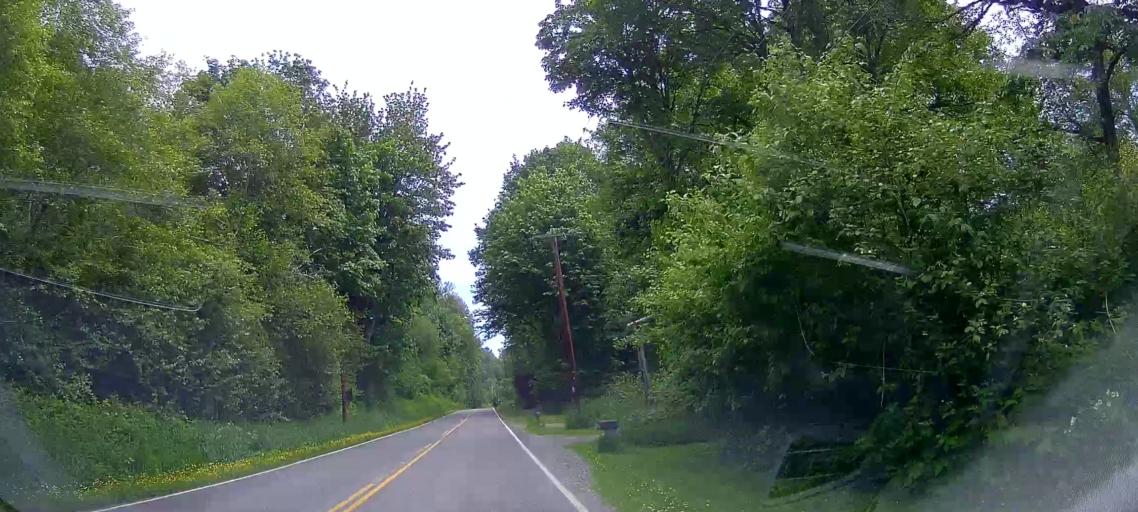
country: US
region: Washington
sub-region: Snohomish County
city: Bryant
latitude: 48.2367
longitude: -122.2115
